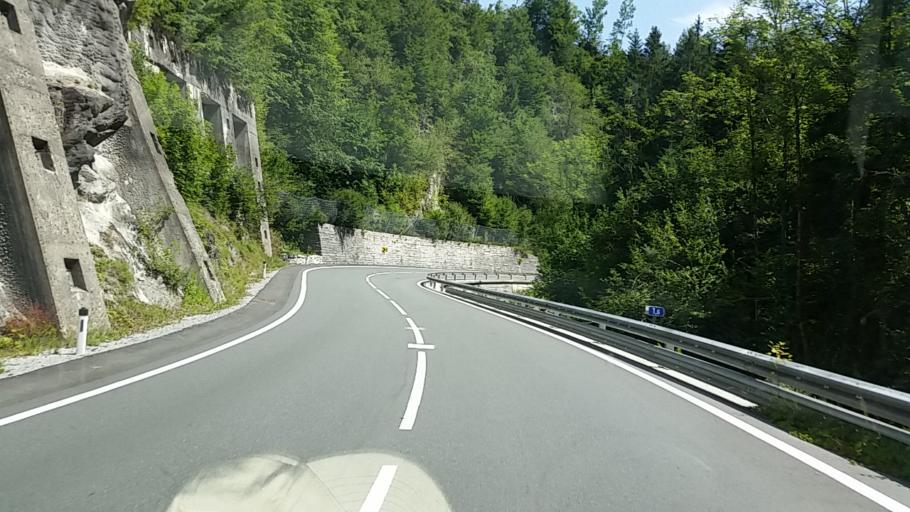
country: AT
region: Salzburg
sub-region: Politischer Bezirk Sankt Johann im Pongau
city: Bischofshofen
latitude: 47.4352
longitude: 13.2278
